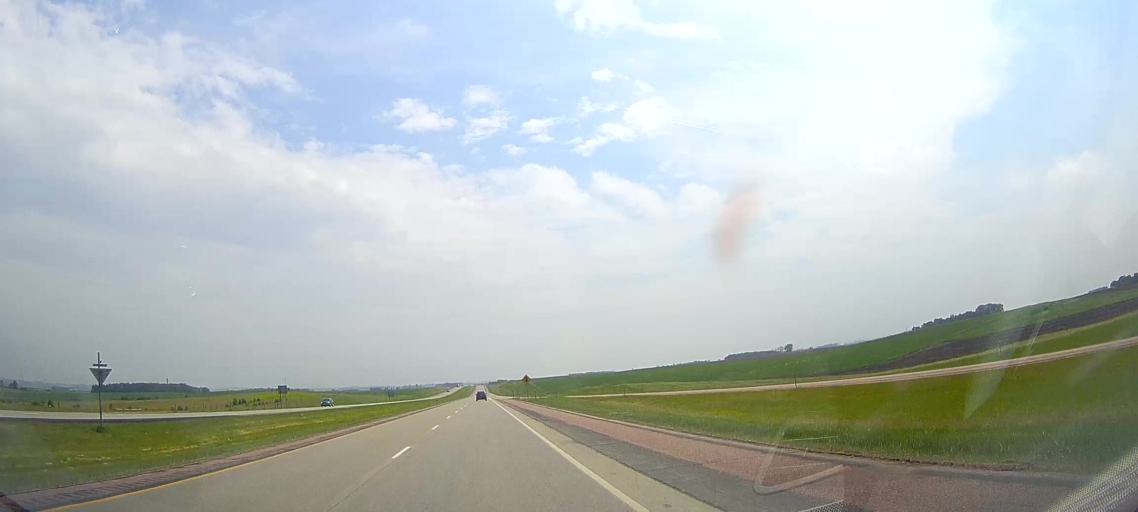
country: US
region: South Dakota
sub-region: Union County
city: Beresford
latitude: 43.0092
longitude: -96.7959
